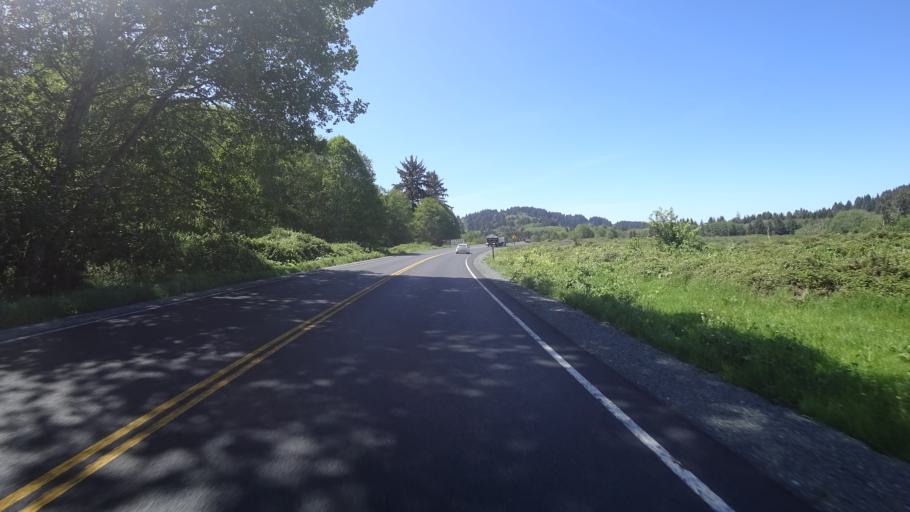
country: US
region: California
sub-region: Humboldt County
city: Westhaven-Moonstone
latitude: 41.2276
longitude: -124.0851
